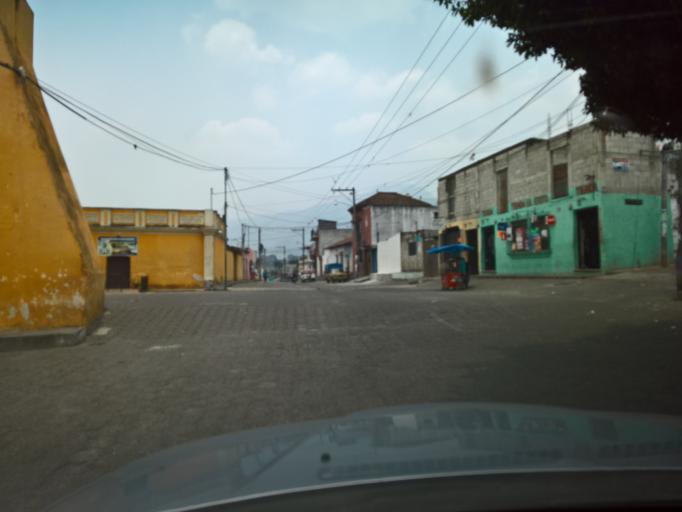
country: GT
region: Sacatepequez
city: Ciudad Vieja
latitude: 14.5263
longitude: -90.7515
